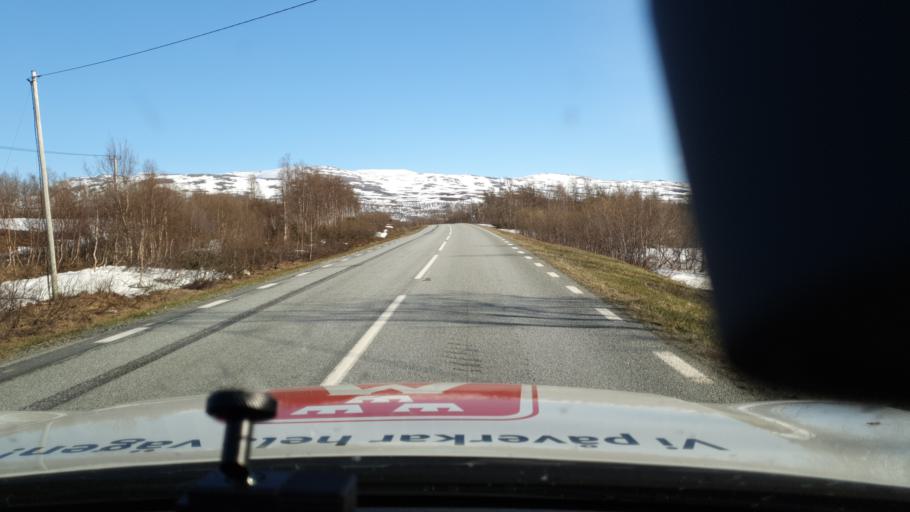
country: NO
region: Nordland
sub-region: Rana
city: Mo i Rana
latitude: 66.0226
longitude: 15.0864
